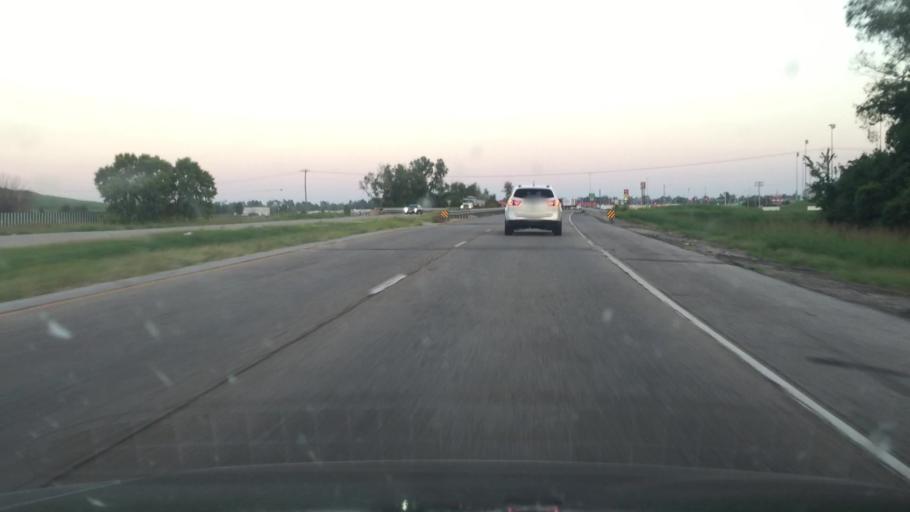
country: US
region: Illinois
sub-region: Madison County
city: Madison
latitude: 38.6577
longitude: -90.1357
